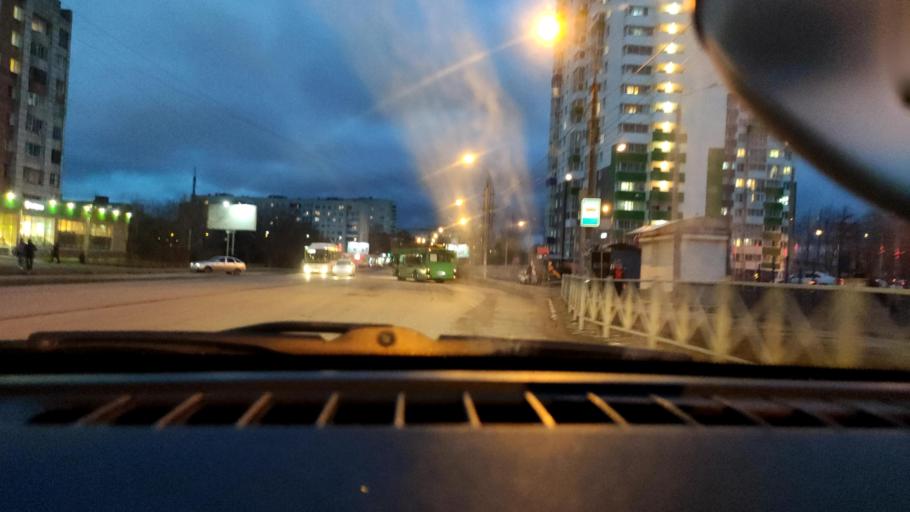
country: RU
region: Perm
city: Perm
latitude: 57.9699
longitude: 56.2288
